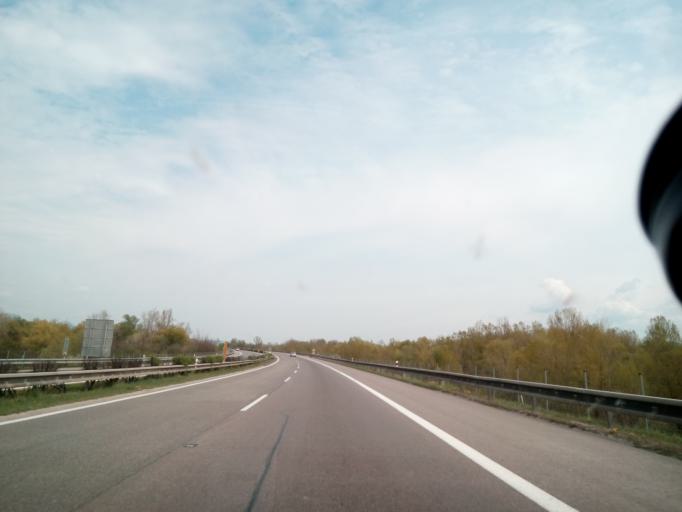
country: SK
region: Trenciansky
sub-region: Okres Trencin
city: Trencin
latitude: 48.9247
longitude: 18.0795
